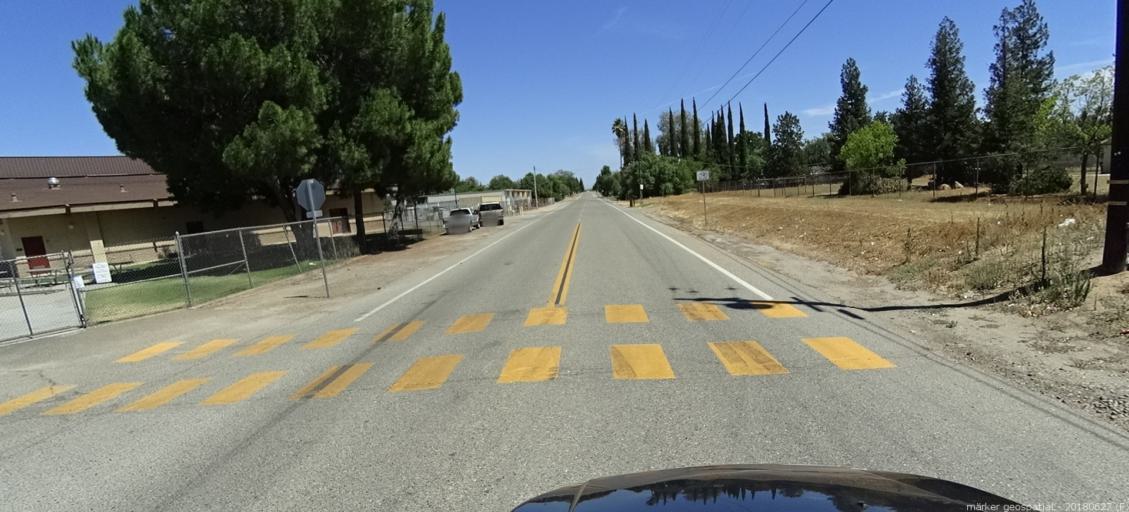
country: US
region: California
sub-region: Madera County
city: Bonadelle Ranchos-Madera Ranchos
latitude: 36.9297
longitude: -119.8851
